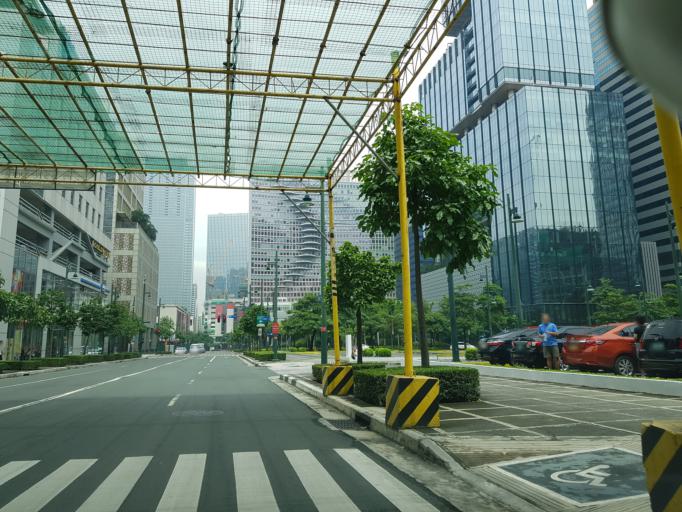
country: PH
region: Metro Manila
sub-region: Makati City
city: Makati City
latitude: 14.5513
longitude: 121.0526
